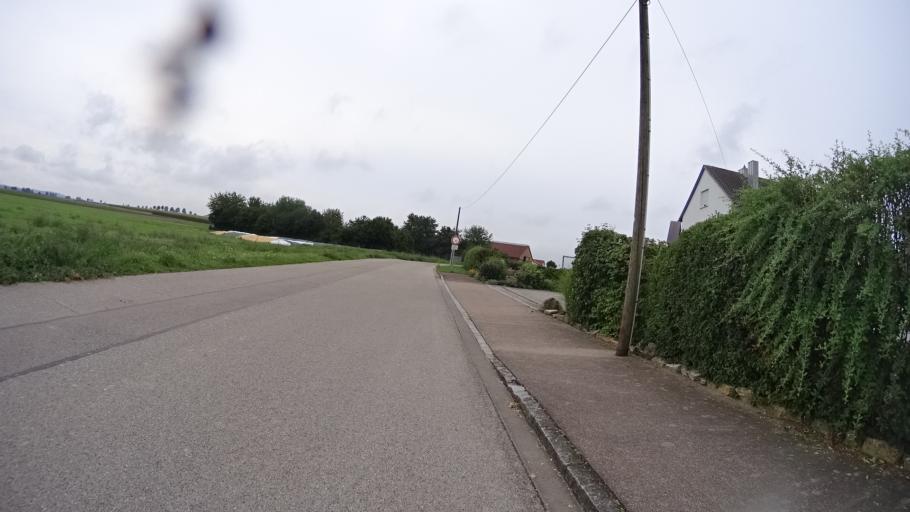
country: DE
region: Bavaria
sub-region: Upper Bavaria
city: Gaimersheim
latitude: 48.8328
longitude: 11.3578
